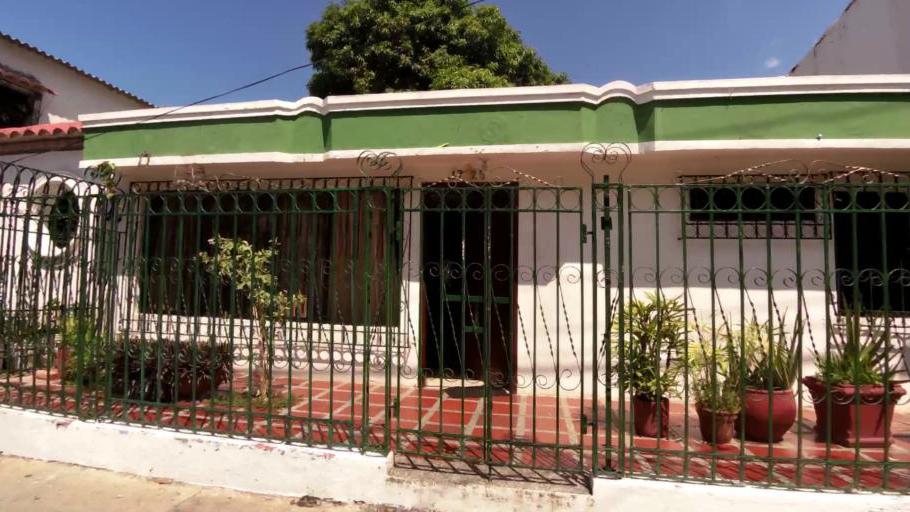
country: CO
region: Bolivar
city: Cartagena
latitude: 10.4147
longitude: -75.5423
